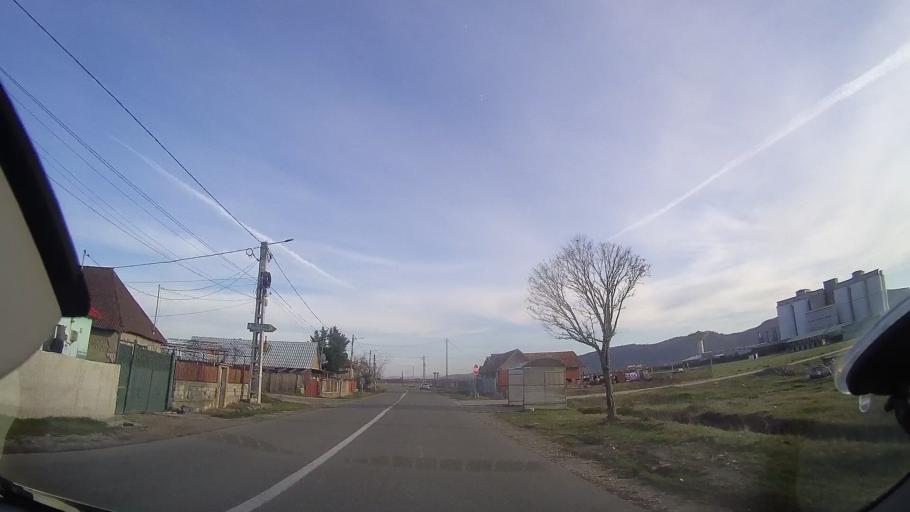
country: RO
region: Bihor
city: Lugasu de Jos
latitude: 47.0444
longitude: 22.3337
